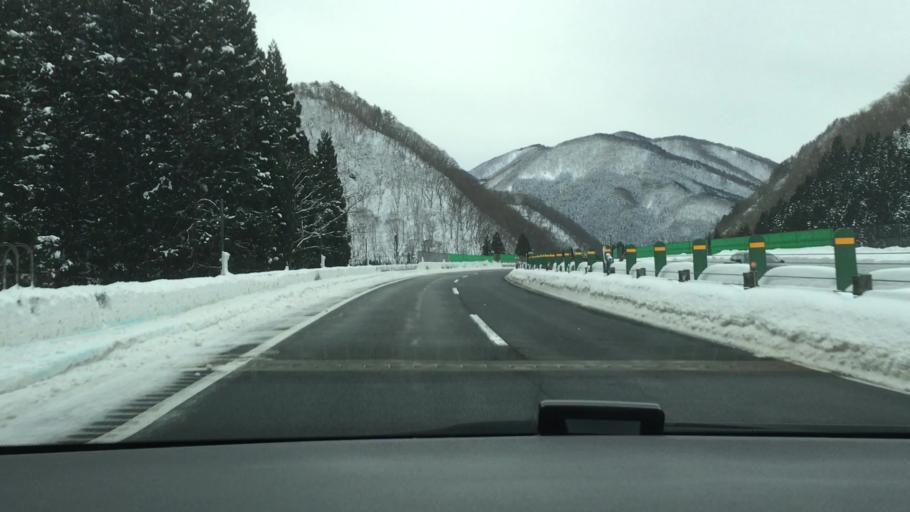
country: JP
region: Akita
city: Hanawa
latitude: 40.1225
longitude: 140.9063
